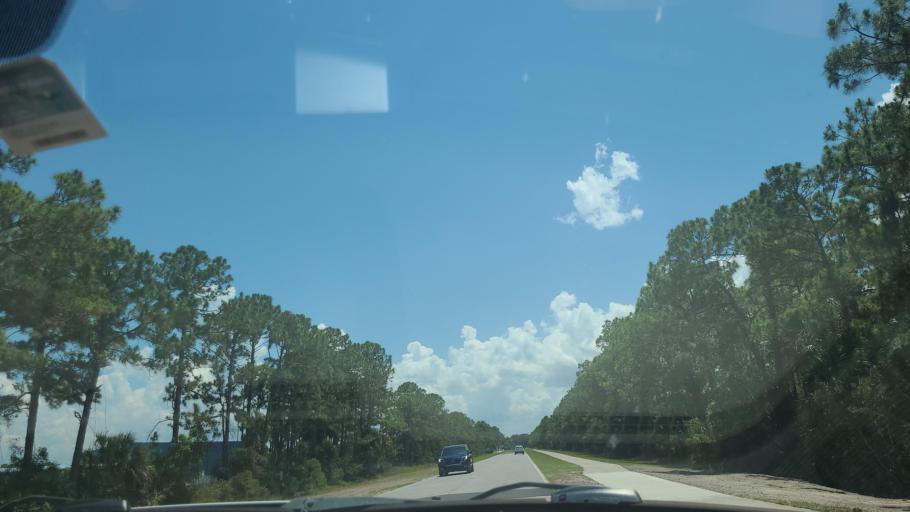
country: US
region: Florida
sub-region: Brevard County
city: Grant-Valkaria
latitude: 27.9623
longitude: -80.5660
